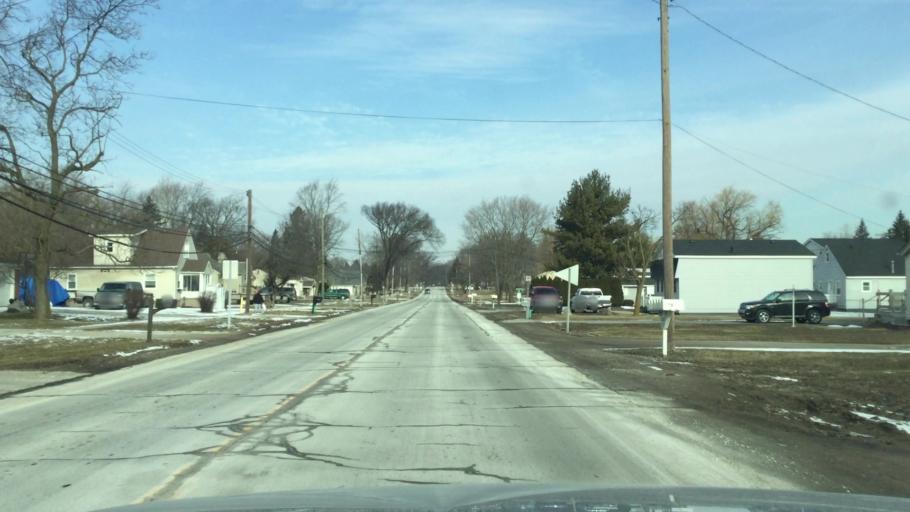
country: US
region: Michigan
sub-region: Wayne County
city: Flat Rock
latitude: 42.1011
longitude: -83.2955
